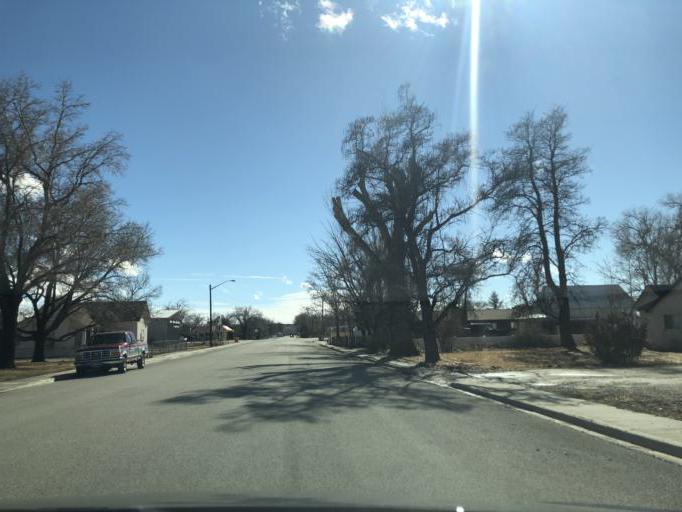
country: US
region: Utah
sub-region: Carbon County
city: East Carbon City
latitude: 38.9968
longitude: -110.1622
